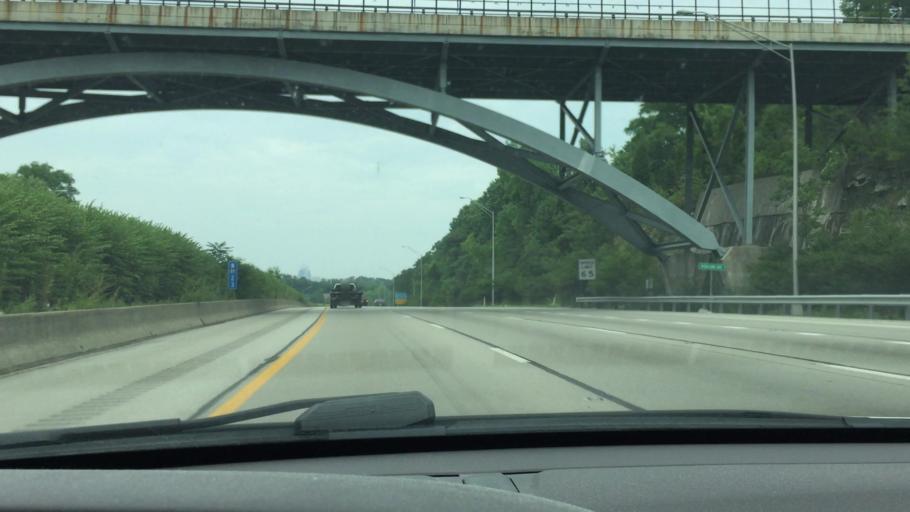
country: US
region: Kentucky
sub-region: Campbell County
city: Southgate
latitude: 39.0736
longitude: -84.4649
